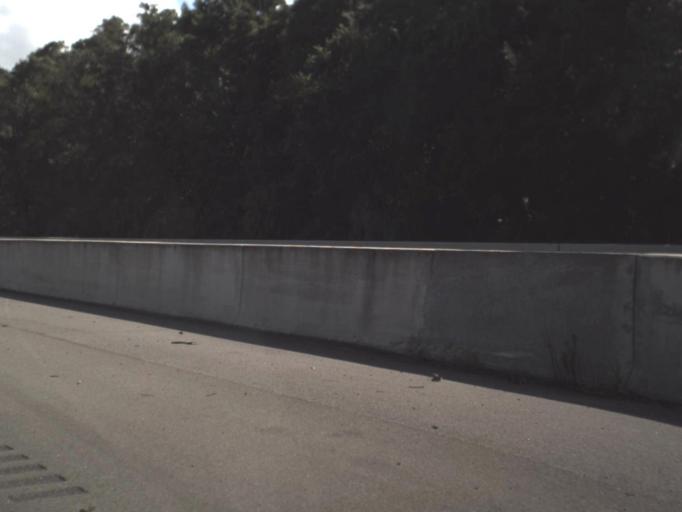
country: US
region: Florida
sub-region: Hillsborough County
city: Pebble Creek
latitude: 28.1833
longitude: -82.3885
